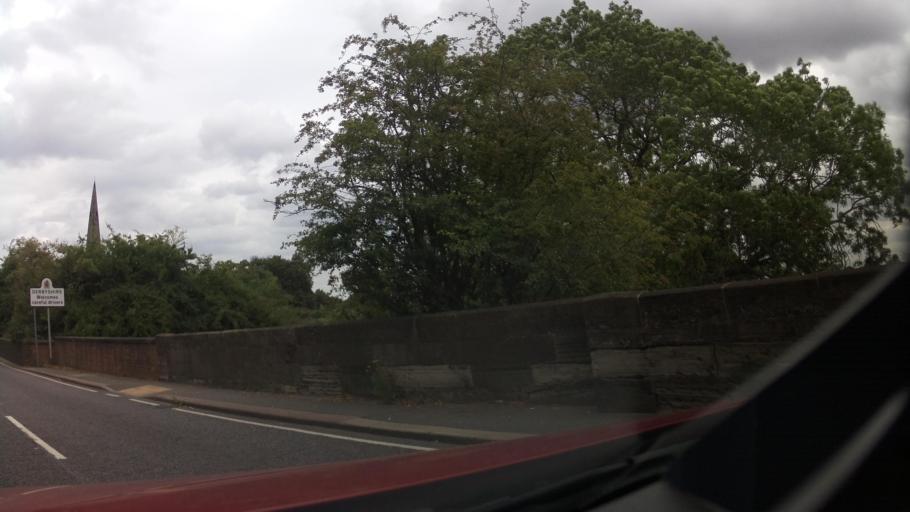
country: GB
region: England
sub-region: Derbyshire
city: Long Eaton
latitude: 52.8760
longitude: -1.3011
